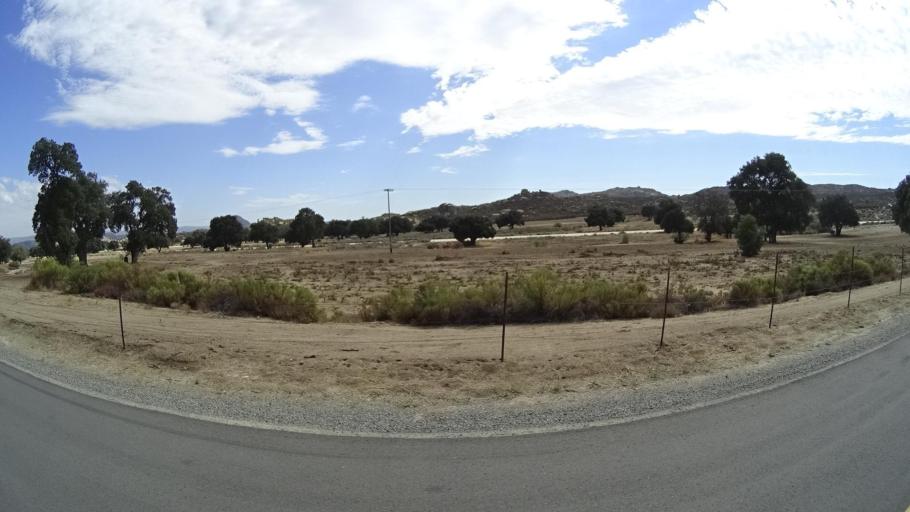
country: MX
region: Baja California
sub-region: Tecate
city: Cereso del Hongo
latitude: 32.6449
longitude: -116.2811
